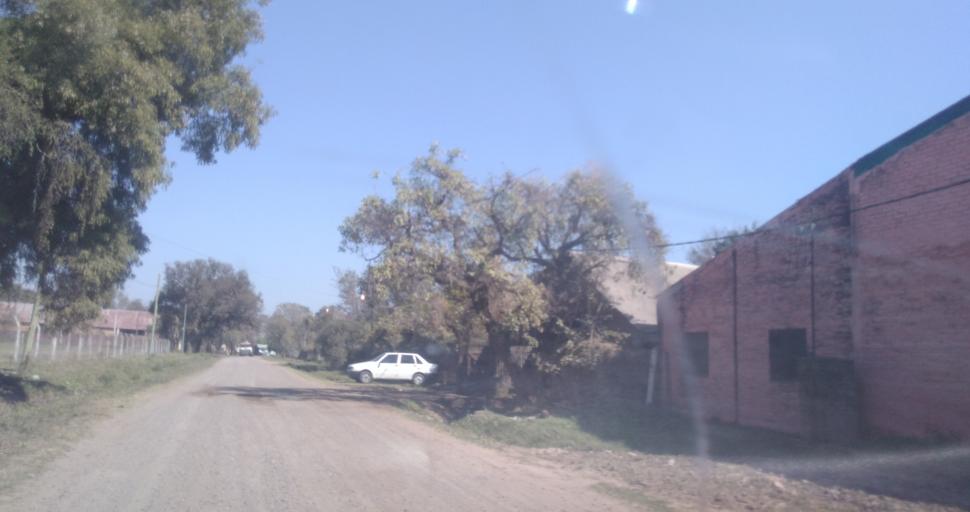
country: AR
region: Chaco
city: Fontana
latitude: -27.4305
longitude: -59.0299
